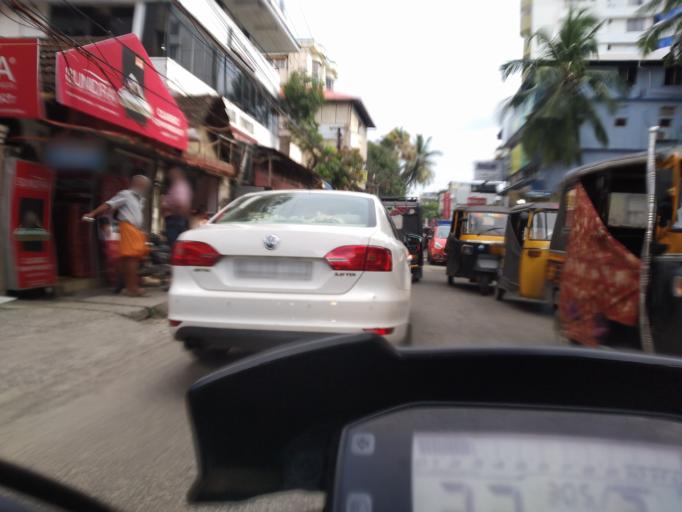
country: IN
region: Kerala
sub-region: Ernakulam
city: Cochin
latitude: 9.9837
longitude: 76.2838
